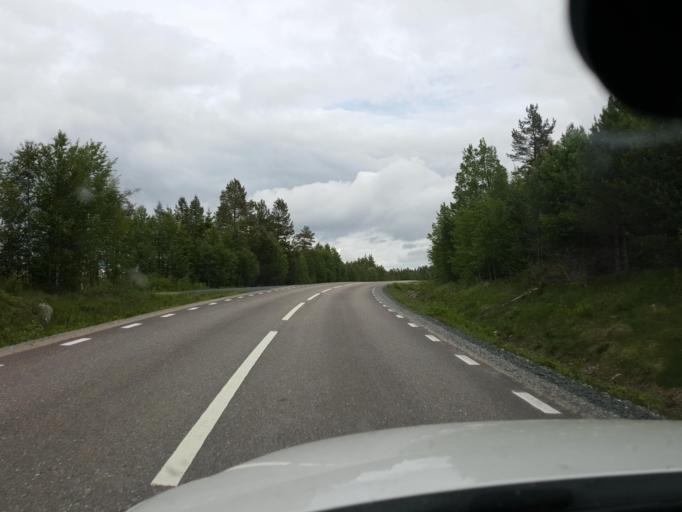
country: SE
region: Gaevleborg
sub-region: Ljusdals Kommun
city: Farila
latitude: 61.7560
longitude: 15.3795
